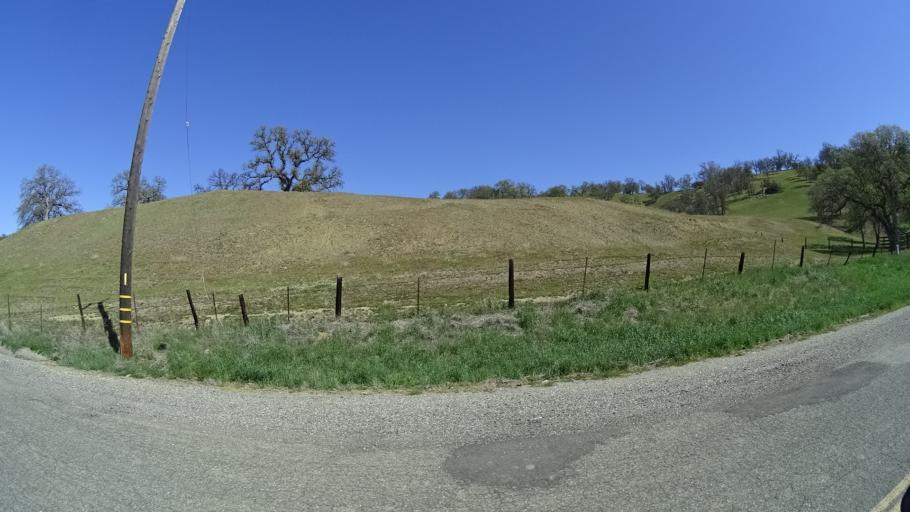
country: US
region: California
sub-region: Tehama County
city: Rancho Tehama Reserve
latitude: 39.7921
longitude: -122.5118
